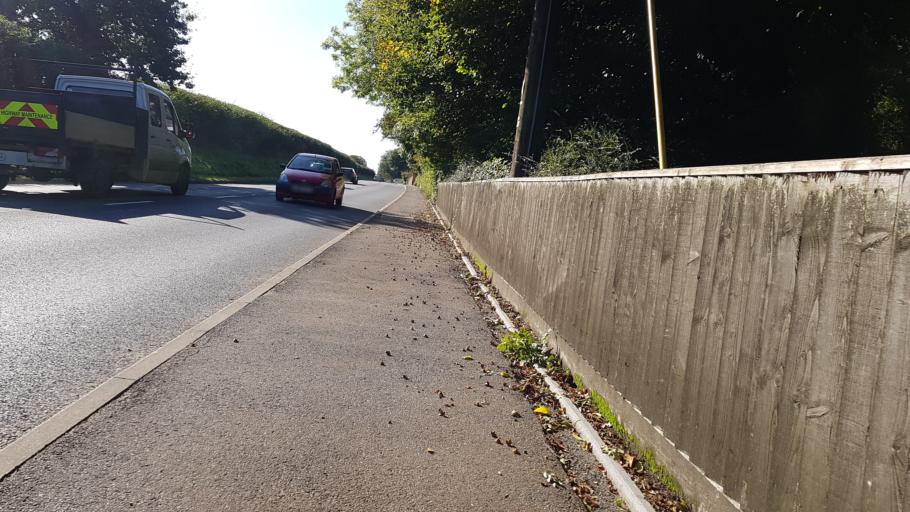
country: GB
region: England
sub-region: Isle of Wight
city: Newport
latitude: 50.6881
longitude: -1.2885
